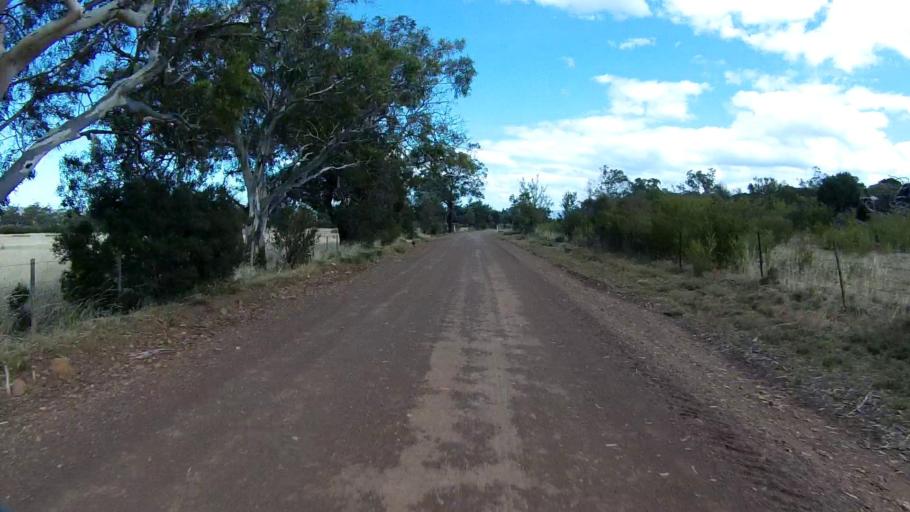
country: AU
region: Tasmania
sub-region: Break O'Day
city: St Helens
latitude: -41.9776
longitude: 148.0696
